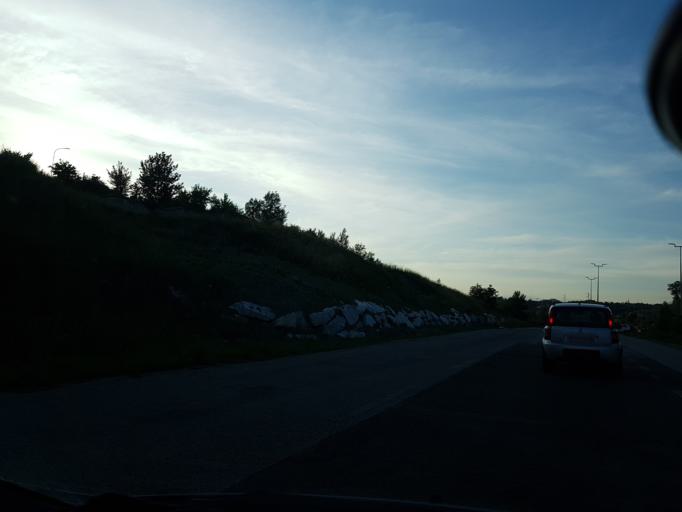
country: IT
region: Tuscany
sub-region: Provincia di Massa-Carrara
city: Aulla
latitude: 44.2178
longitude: 9.9767
